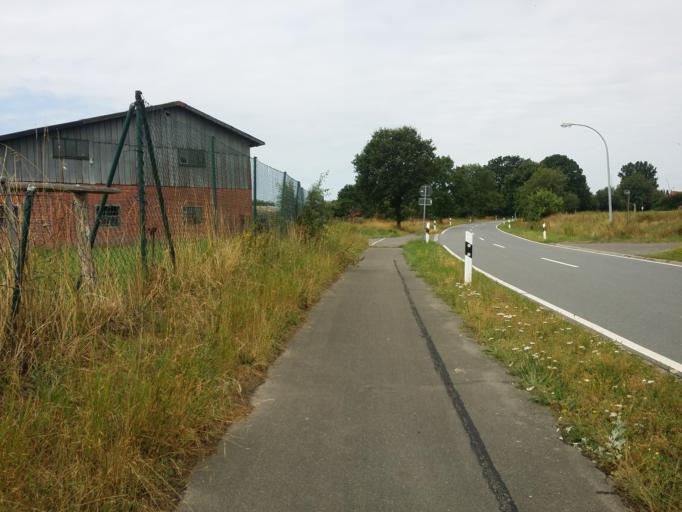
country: DE
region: Schleswig-Holstein
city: Huje
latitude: 53.9725
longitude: 9.4394
